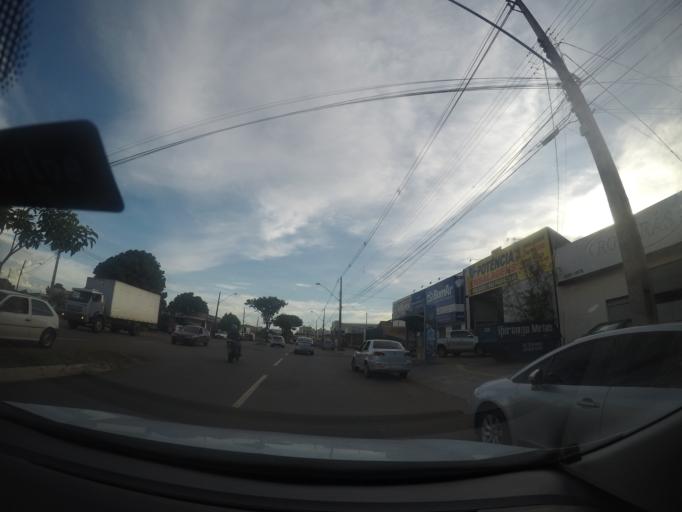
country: BR
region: Goias
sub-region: Goiania
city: Goiania
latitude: -16.6820
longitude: -49.3201
